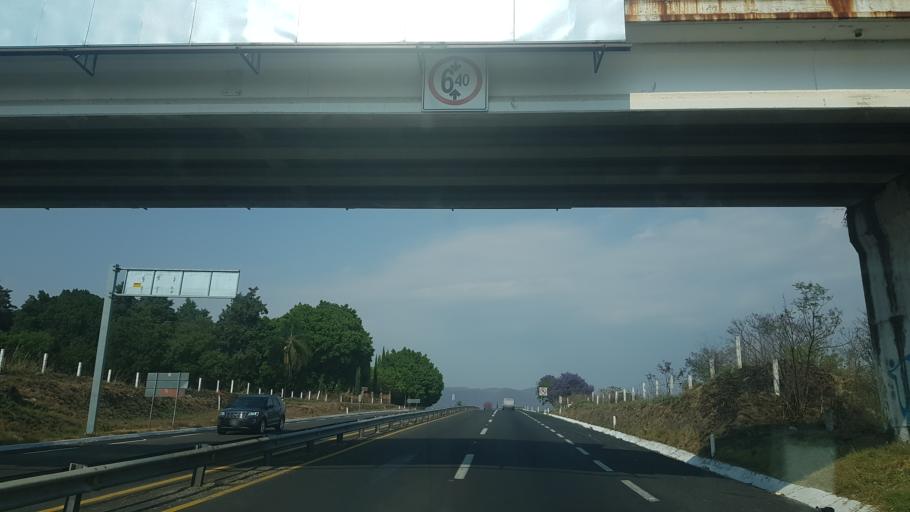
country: MX
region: Puebla
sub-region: Atlixco
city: San Agustin Huixaxtla
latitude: 18.9231
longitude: -98.4037
